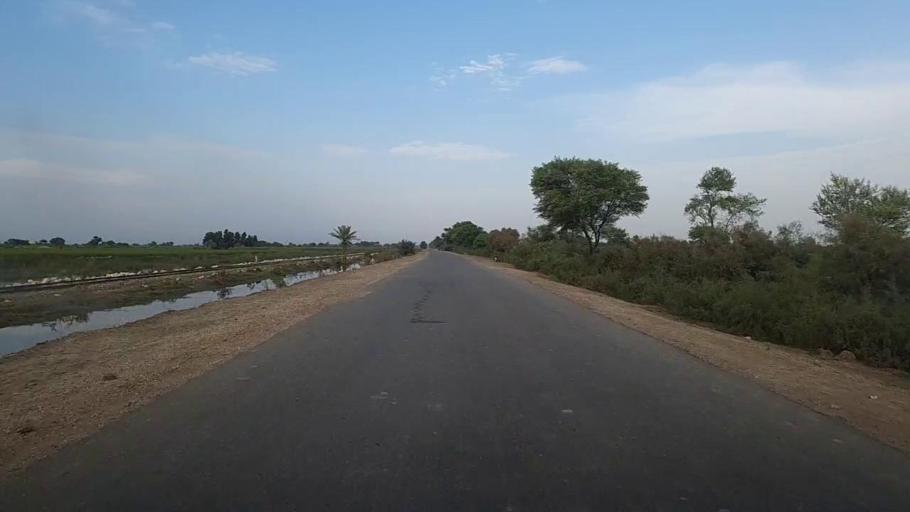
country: PK
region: Sindh
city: Thul
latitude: 28.2857
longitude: 68.8632
